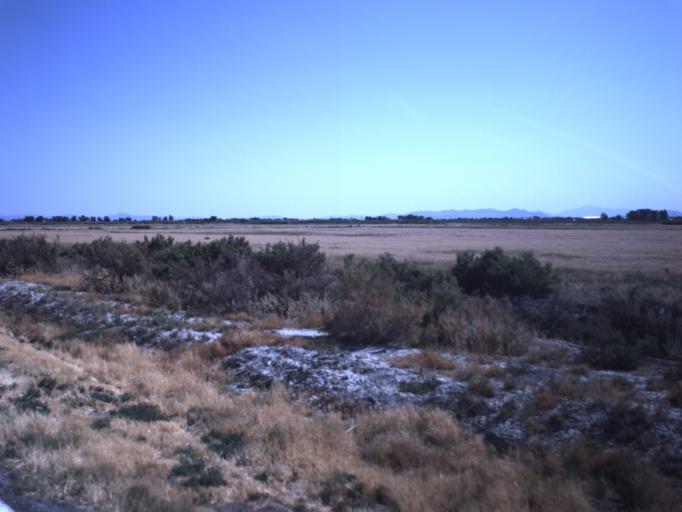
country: US
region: Utah
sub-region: Millard County
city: Delta
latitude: 39.3101
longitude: -112.6525
